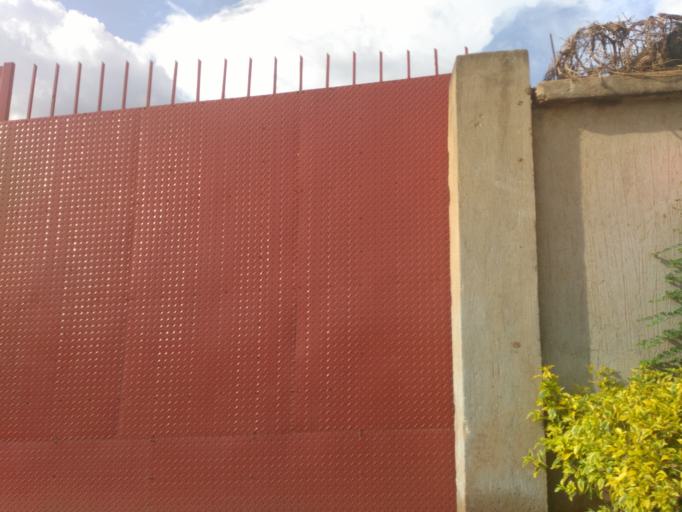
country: UG
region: Eastern Region
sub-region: Jinja District
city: Jinja
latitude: 0.4163
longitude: 33.2185
